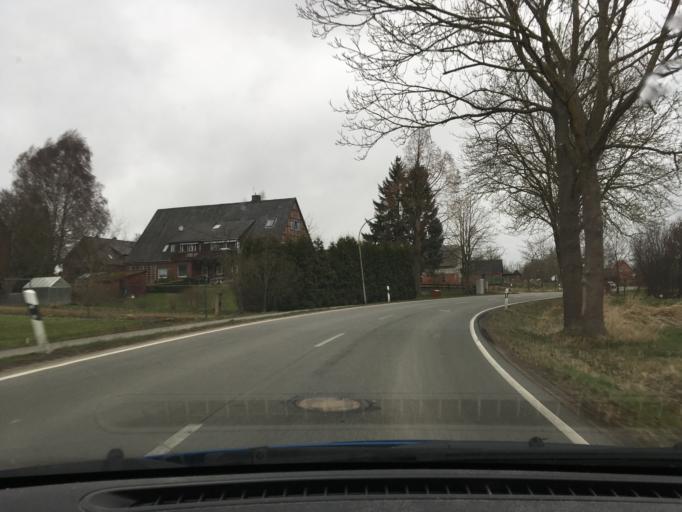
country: DE
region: Lower Saxony
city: Drage
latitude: 53.4087
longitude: 10.2606
